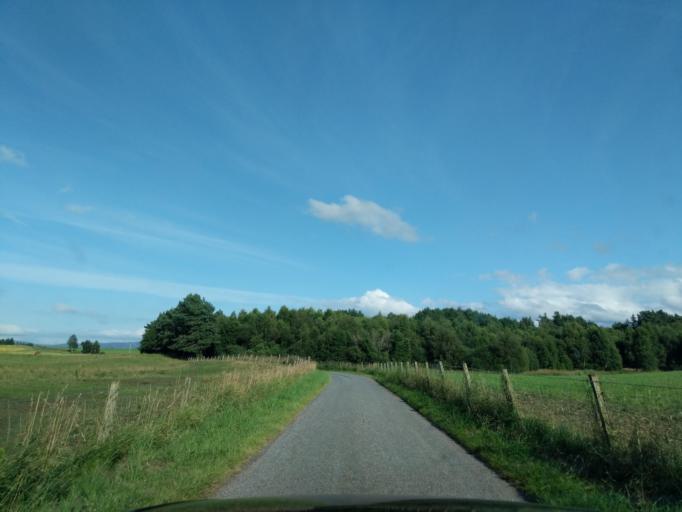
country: GB
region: Scotland
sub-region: Highland
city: Aviemore
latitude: 57.2910
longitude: -3.7508
